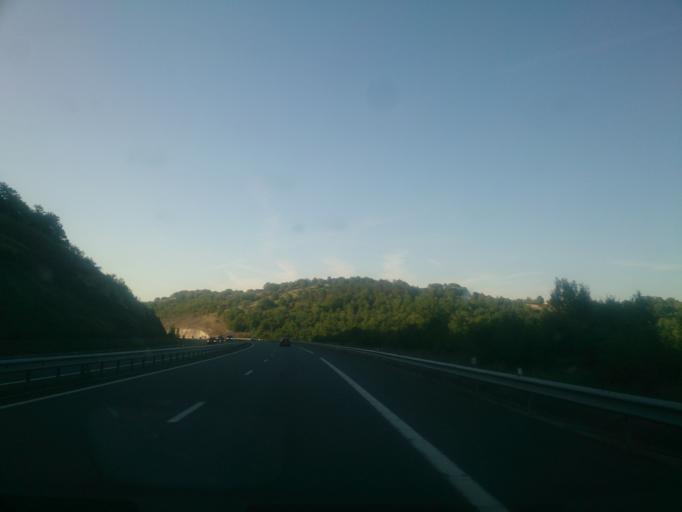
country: FR
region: Midi-Pyrenees
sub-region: Departement du Lot
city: Le Vigan
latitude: 44.7360
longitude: 1.5557
